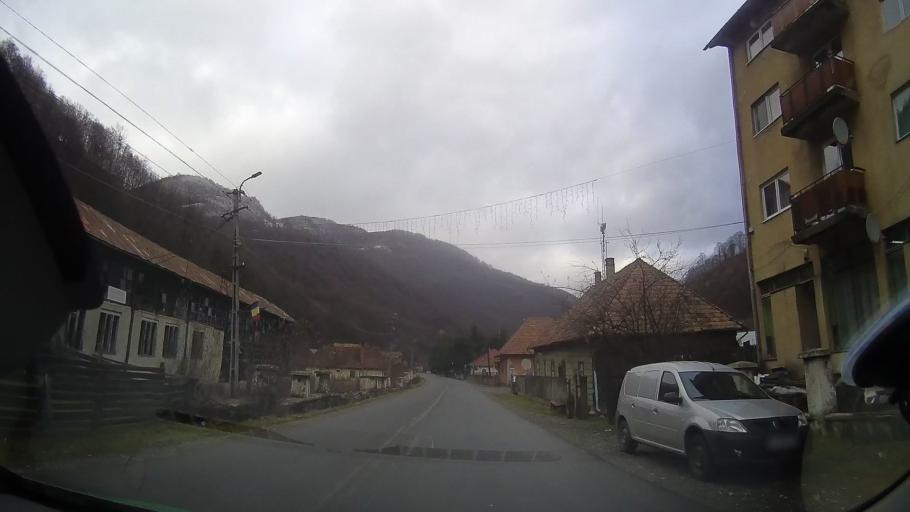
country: RO
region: Cluj
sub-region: Comuna Maguri-Racatau
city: Maguri-Racatau
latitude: 46.6472
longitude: 23.1963
